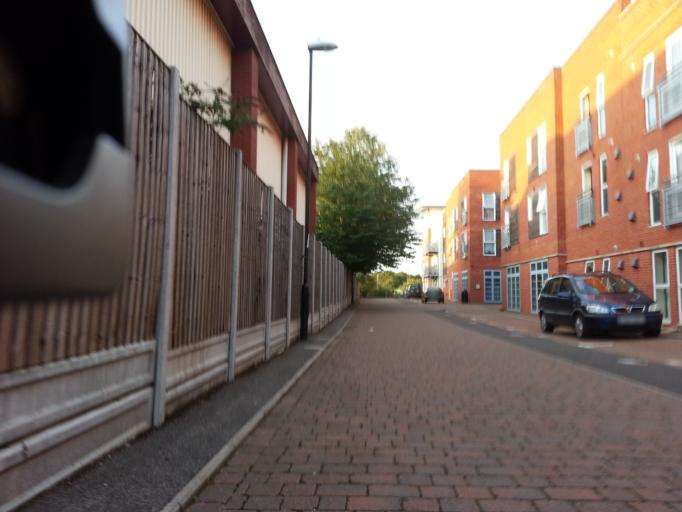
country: GB
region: England
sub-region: Suffolk
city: Ipswich
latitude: 52.0532
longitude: 1.1370
